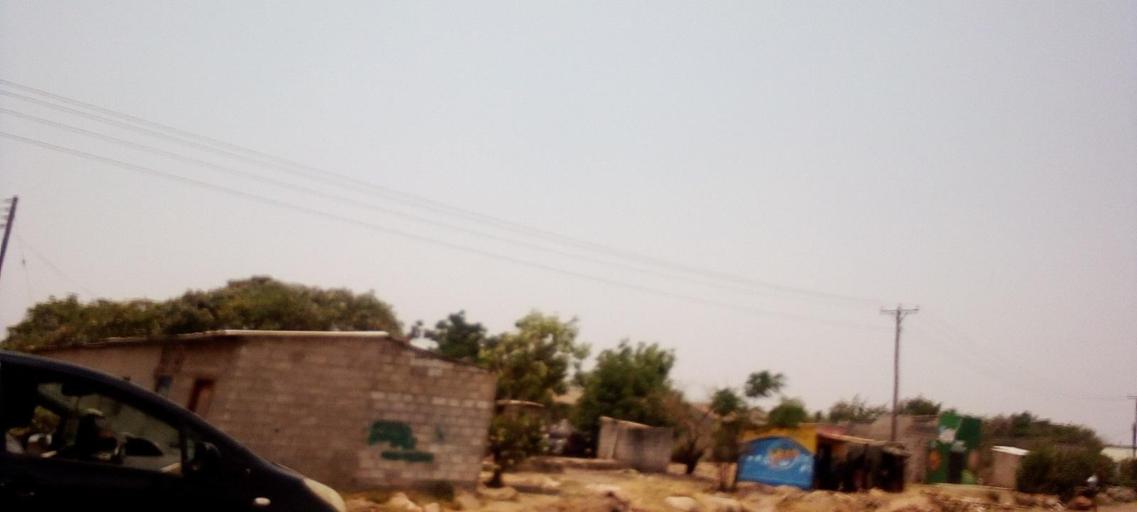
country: ZM
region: Lusaka
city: Lusaka
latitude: -15.4430
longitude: 28.2499
